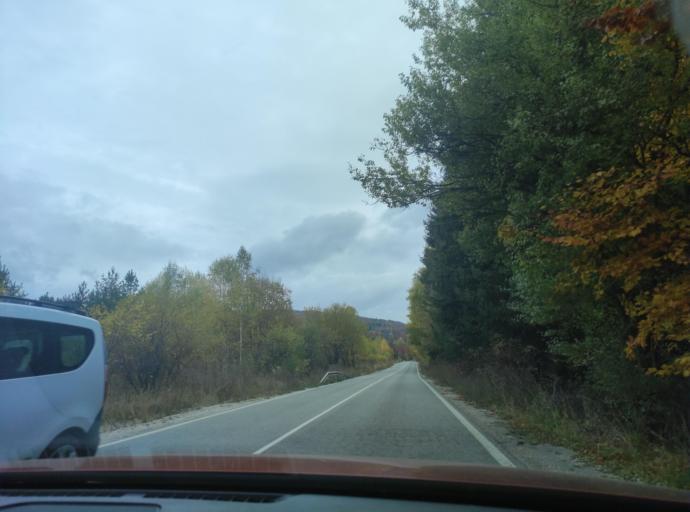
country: BG
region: Sofiya
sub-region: Obshtina Godech
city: Godech
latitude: 43.0994
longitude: 23.1012
